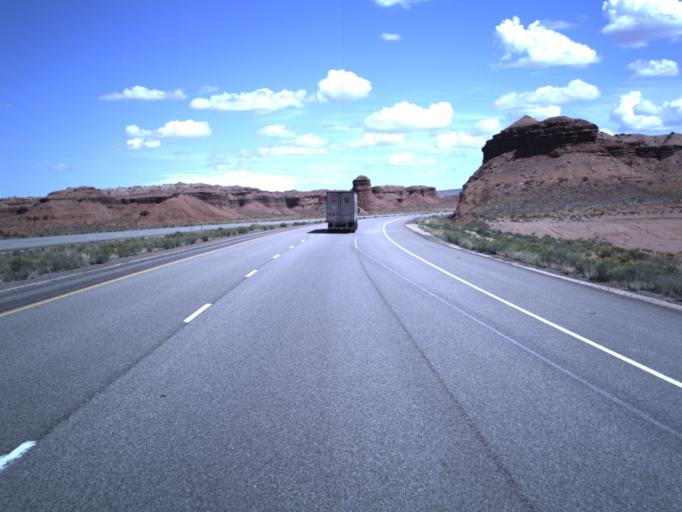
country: US
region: Utah
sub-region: Emery County
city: Ferron
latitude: 38.8443
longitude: -111.0601
